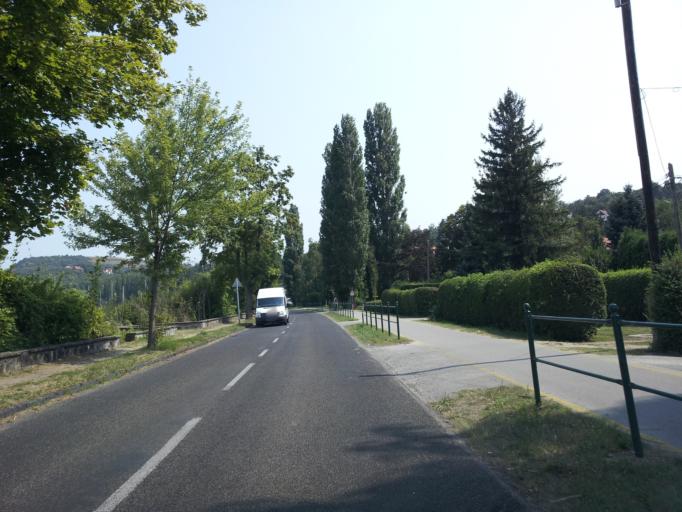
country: HU
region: Veszprem
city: Tihany
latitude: 46.9264
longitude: 17.8630
